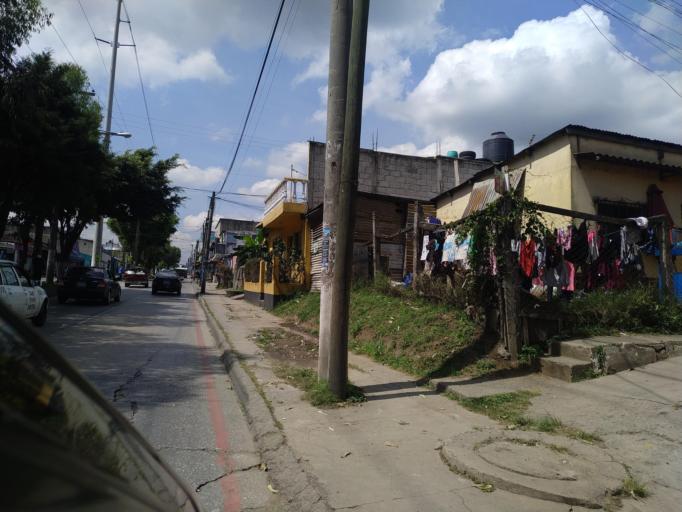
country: GT
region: Guatemala
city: Mixco
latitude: 14.6661
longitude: -90.5849
